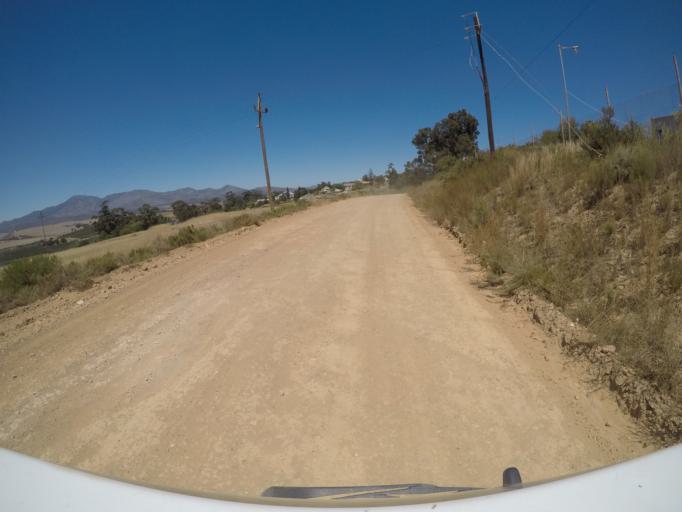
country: ZA
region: Western Cape
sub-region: Overberg District Municipality
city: Hermanus
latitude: -34.2215
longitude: 19.2054
